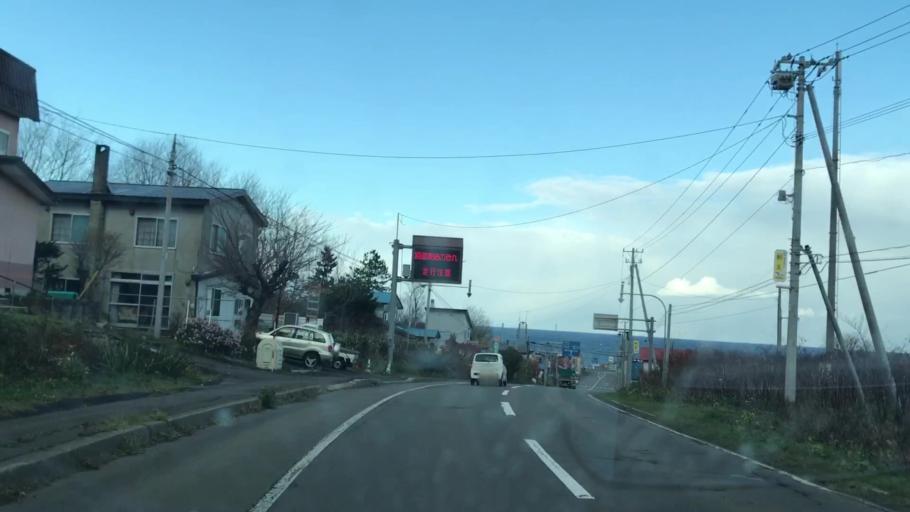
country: JP
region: Hokkaido
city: Yoichi
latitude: 43.3391
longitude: 140.4592
